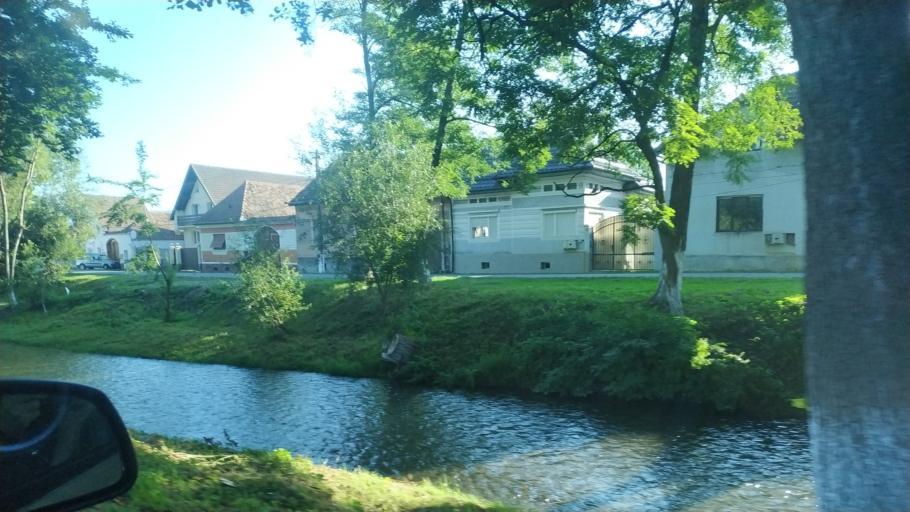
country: RO
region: Brasov
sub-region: Comuna Beclean
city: Beclean
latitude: 45.8306
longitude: 24.9239
